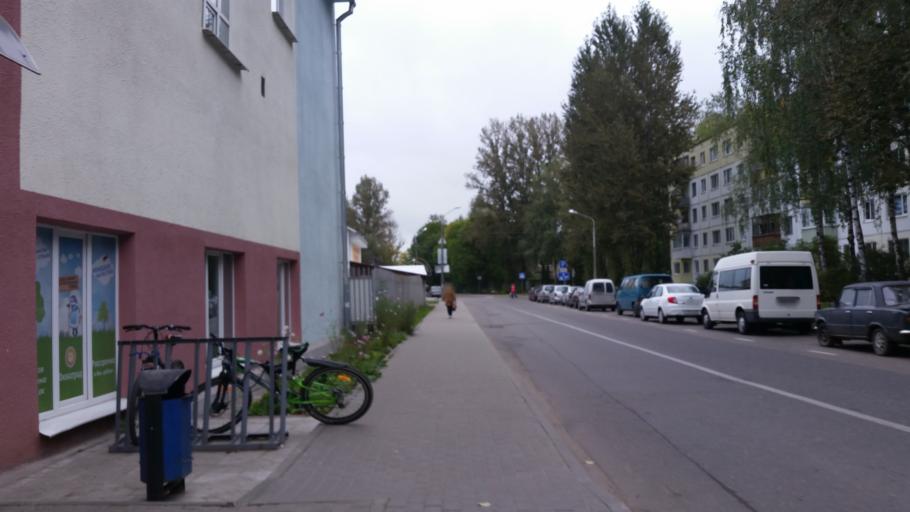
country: BY
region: Vitebsk
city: Vitebsk
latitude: 55.1800
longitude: 30.2235
